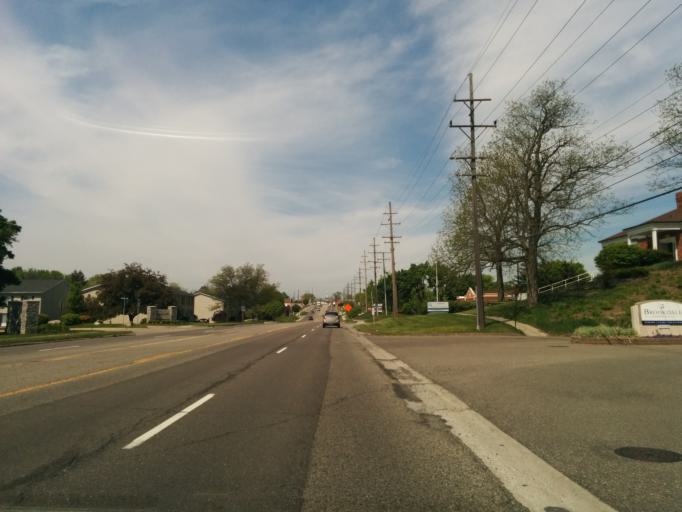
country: US
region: Michigan
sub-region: Oakland County
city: Farmington
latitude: 42.4689
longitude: -83.4078
